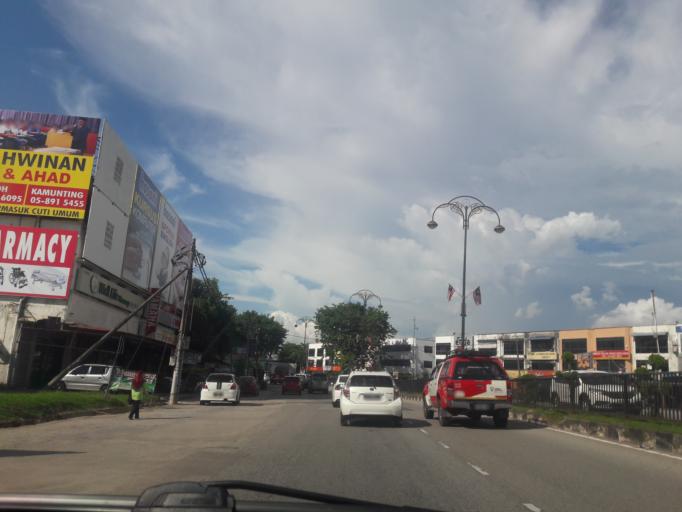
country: MY
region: Kedah
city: Sungai Petani
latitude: 5.6370
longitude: 100.4880
